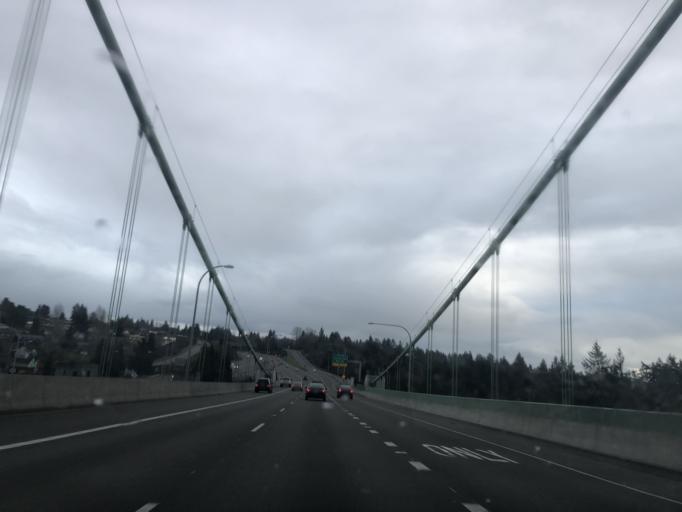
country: US
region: Washington
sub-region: Pierce County
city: University Place
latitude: 47.2635
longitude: -122.5453
